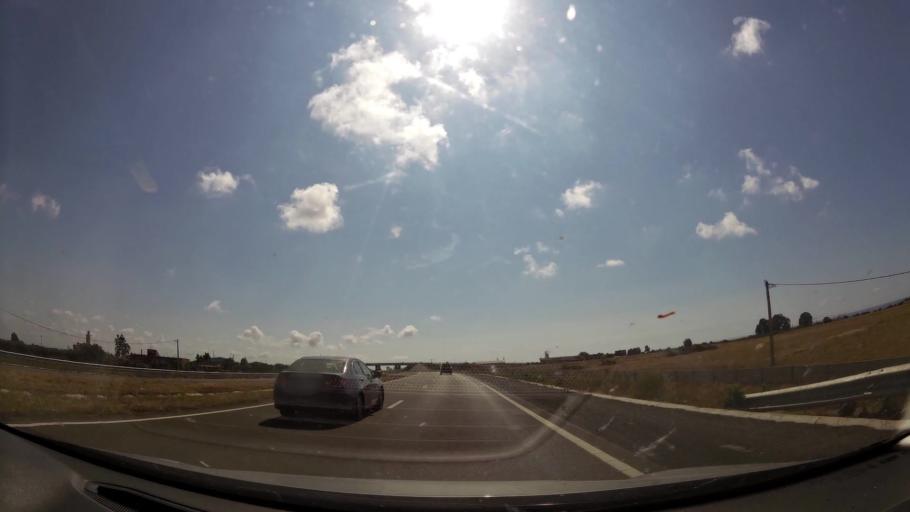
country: MA
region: Rabat-Sale-Zemmour-Zaer
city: Skhirat
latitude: 33.8643
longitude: -6.9614
